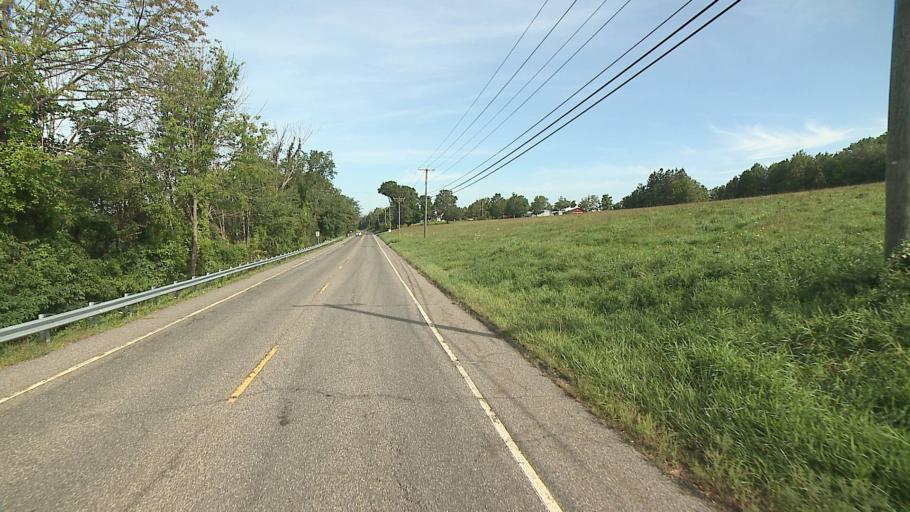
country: US
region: Connecticut
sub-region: Litchfield County
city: Litchfield
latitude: 41.7127
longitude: -73.1377
